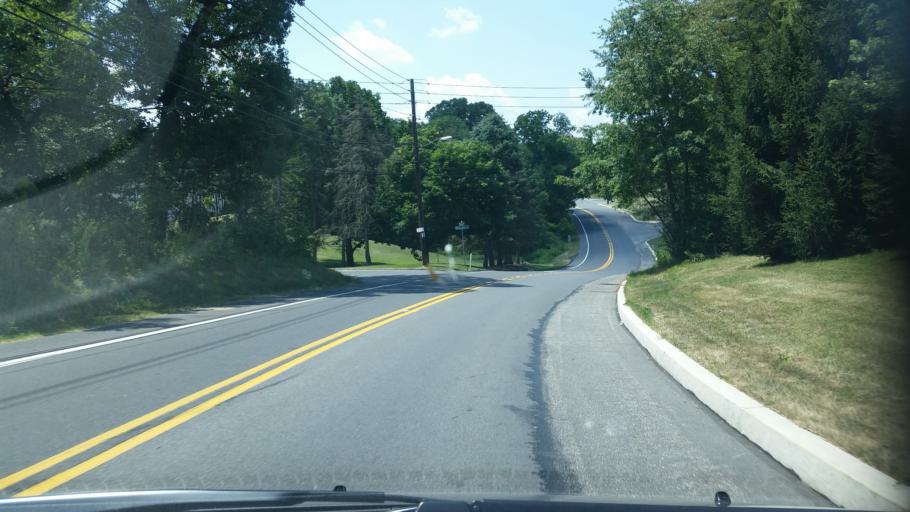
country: US
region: Pennsylvania
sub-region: Dauphin County
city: Rutherford
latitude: 40.2901
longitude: -76.7545
